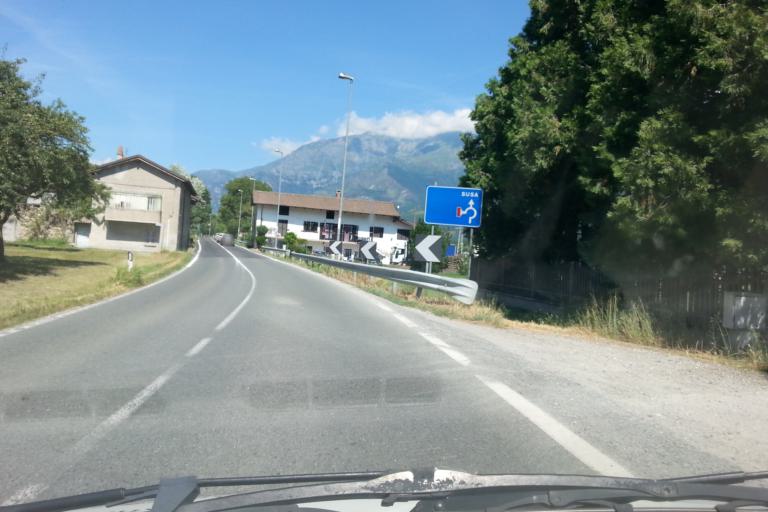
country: IT
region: Piedmont
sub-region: Provincia di Torino
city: Borgone Susa
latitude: 45.1185
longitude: 7.2346
